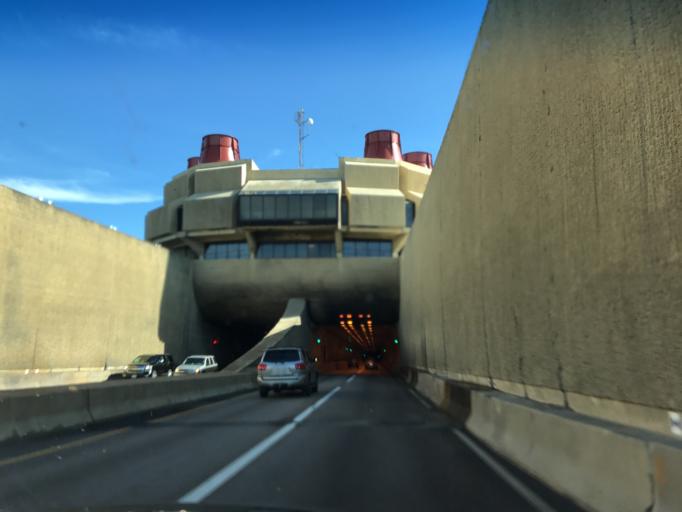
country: US
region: Virginia
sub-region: City of Newport News
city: Newport News
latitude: 36.9606
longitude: -76.4112
